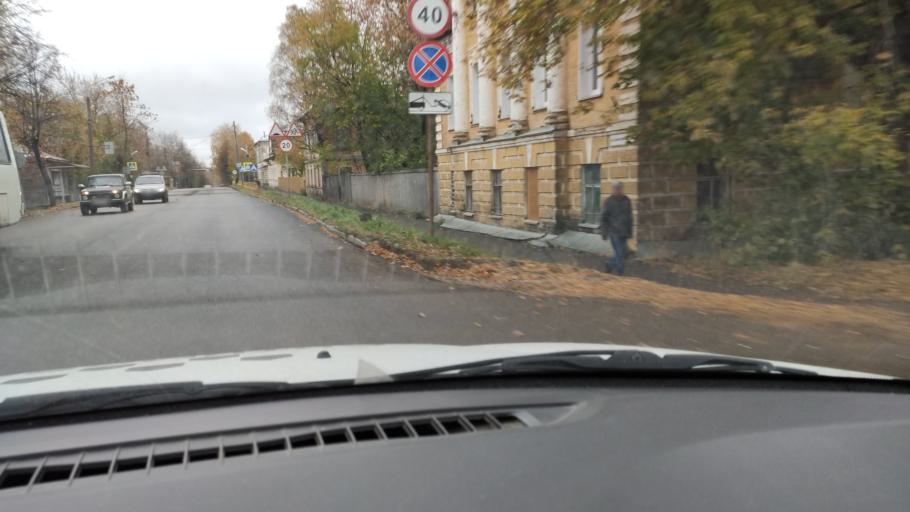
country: RU
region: Kirov
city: Slobodskoy
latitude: 58.7353
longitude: 50.1825
